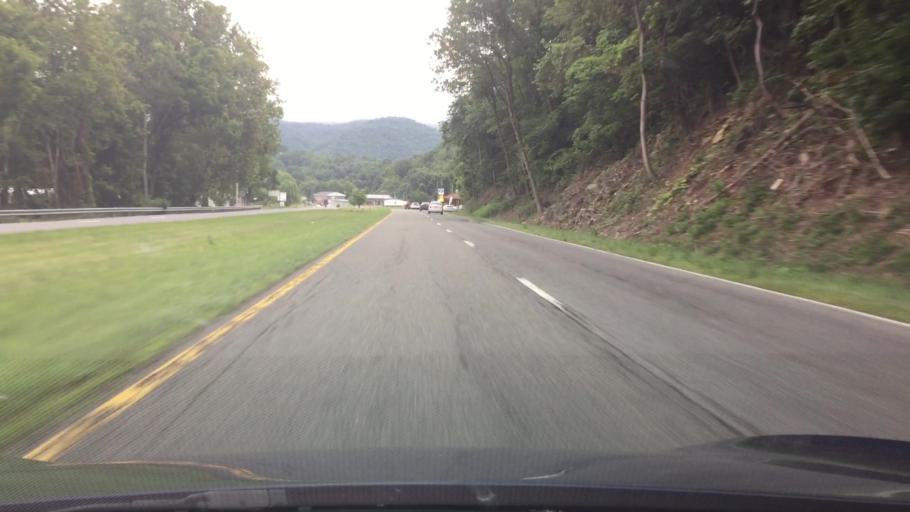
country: US
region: Virginia
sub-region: Montgomery County
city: Shawsville
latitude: 37.1701
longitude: -80.2634
